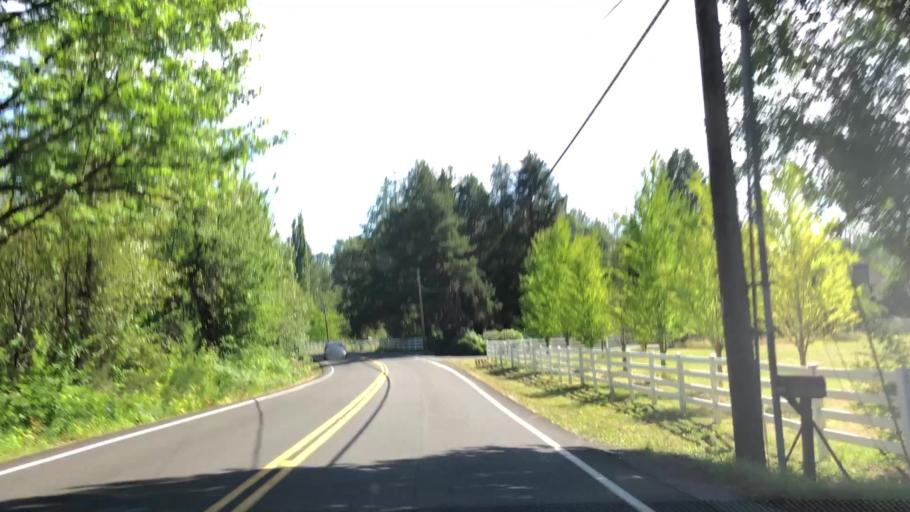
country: US
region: Washington
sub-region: King County
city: Cottage Lake
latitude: 47.7237
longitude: -122.0782
